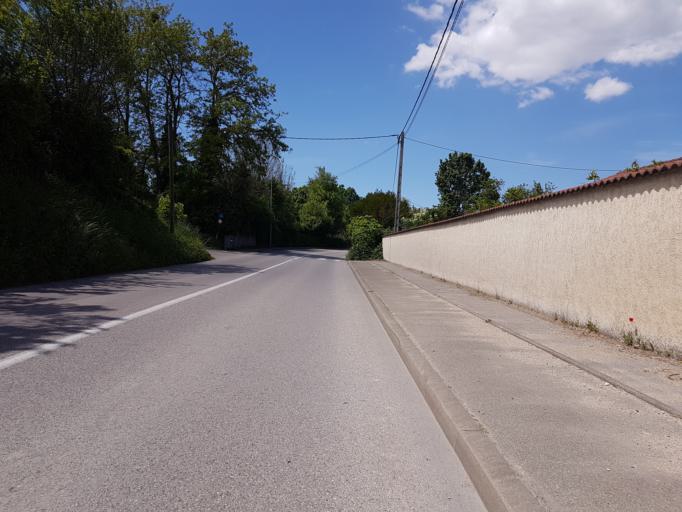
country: FR
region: Rhone-Alpes
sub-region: Departement de l'Isere
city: Chavanoz
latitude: 45.7786
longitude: 5.1734
